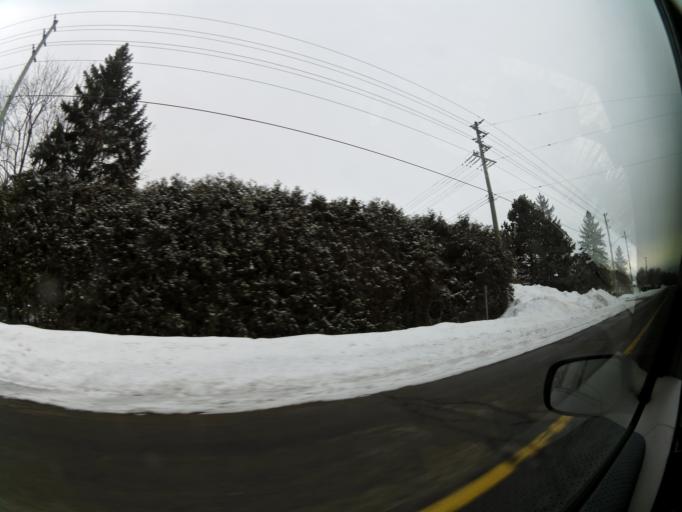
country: CA
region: Quebec
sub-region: Outaouais
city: Gatineau
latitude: 45.4603
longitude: -75.5937
